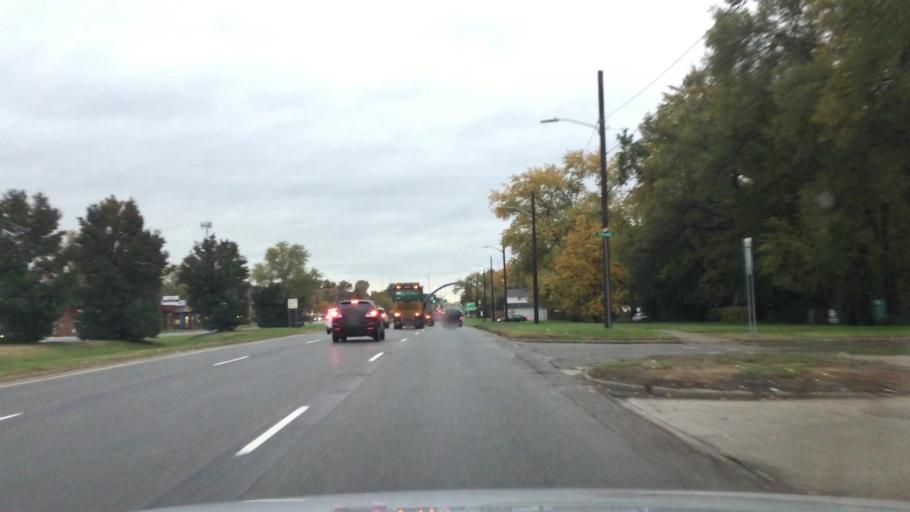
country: US
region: Michigan
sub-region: Wayne County
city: Taylor
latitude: 42.2740
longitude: -83.2708
